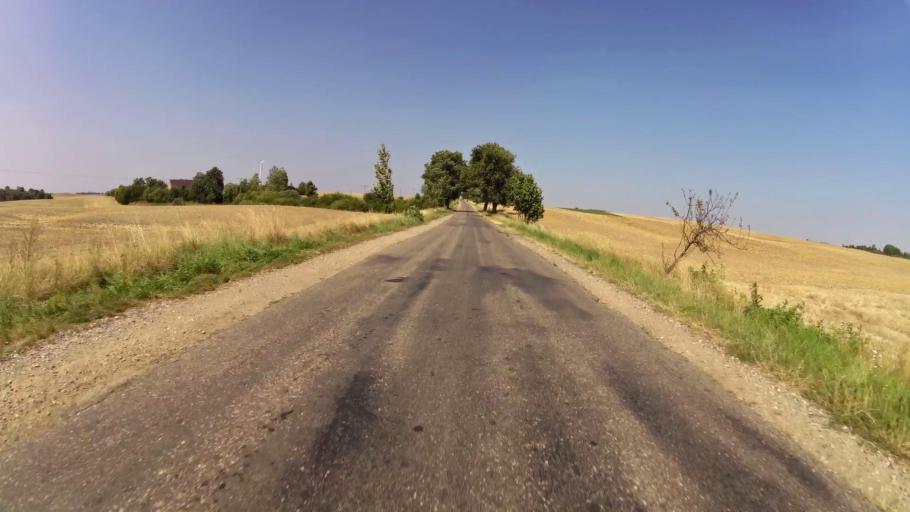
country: PL
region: West Pomeranian Voivodeship
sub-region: Powiat walecki
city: Walcz
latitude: 53.2141
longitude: 16.4778
